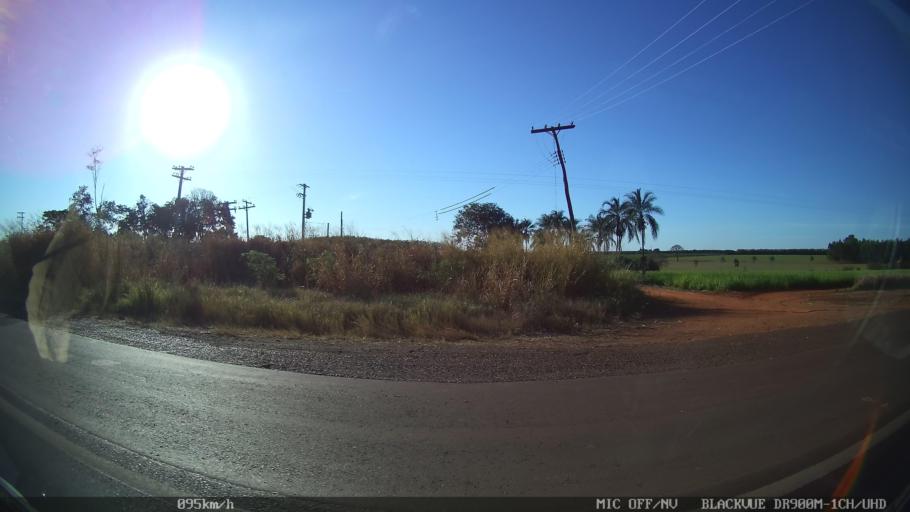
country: BR
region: Sao Paulo
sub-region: Guapiacu
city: Guapiacu
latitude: -20.7505
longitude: -49.1361
